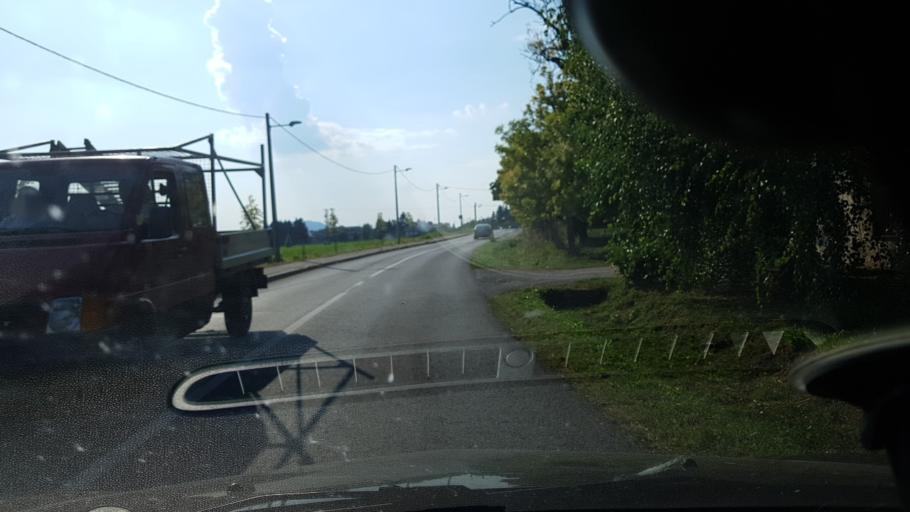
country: HR
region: Zagrebacka
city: Bregana
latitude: 45.8844
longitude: 15.7093
